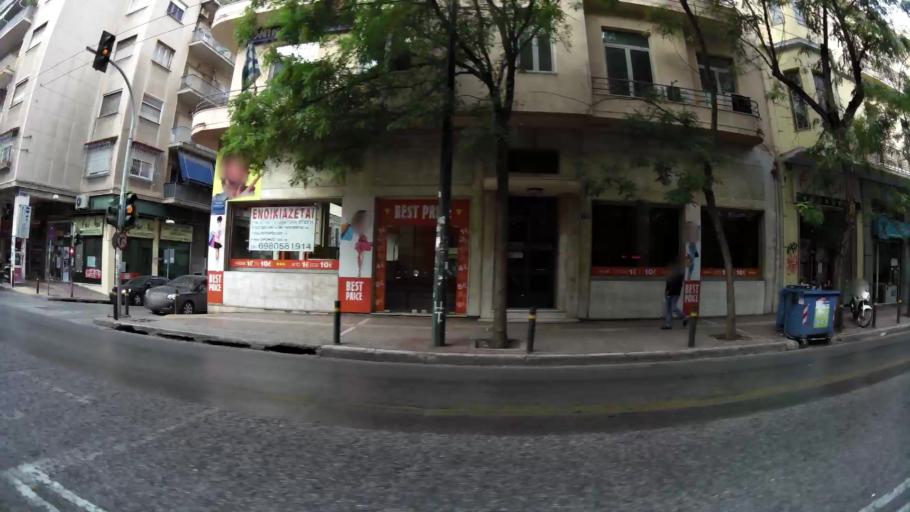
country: GR
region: Attica
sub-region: Nomarchia Athinas
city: Kipseli
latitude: 38.0077
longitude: 23.7349
